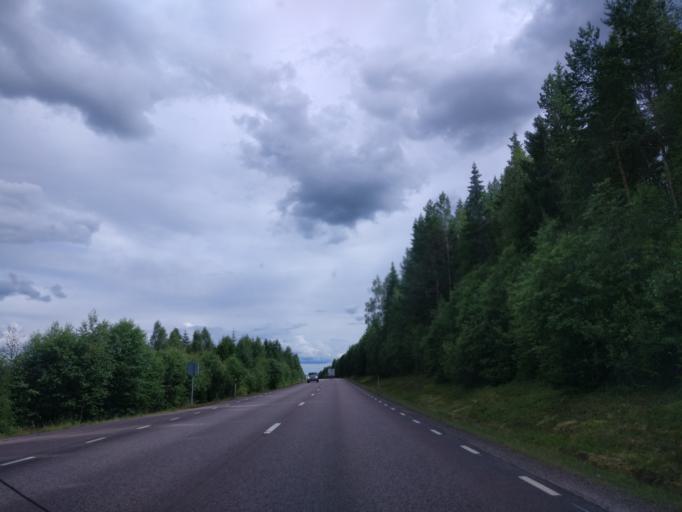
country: SE
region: Vaermland
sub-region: Hagfors Kommun
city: Ekshaerad
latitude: 60.1522
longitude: 13.5183
